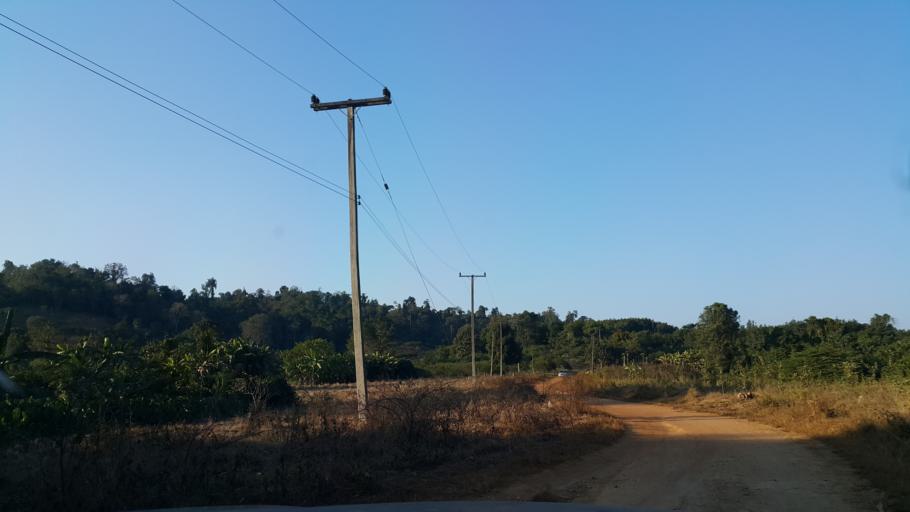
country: TH
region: Sukhothai
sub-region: Amphoe Si Satchanalai
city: Si Satchanalai
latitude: 17.5979
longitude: 99.6137
